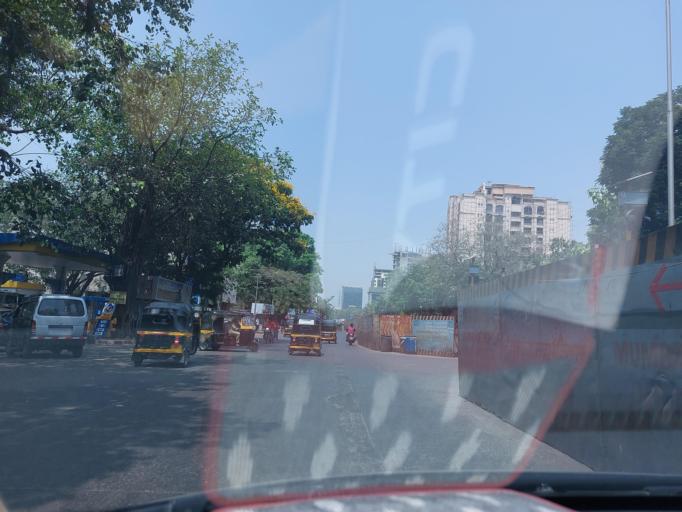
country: IN
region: Maharashtra
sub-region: Mumbai Suburban
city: Mumbai
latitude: 19.0541
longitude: 72.8937
